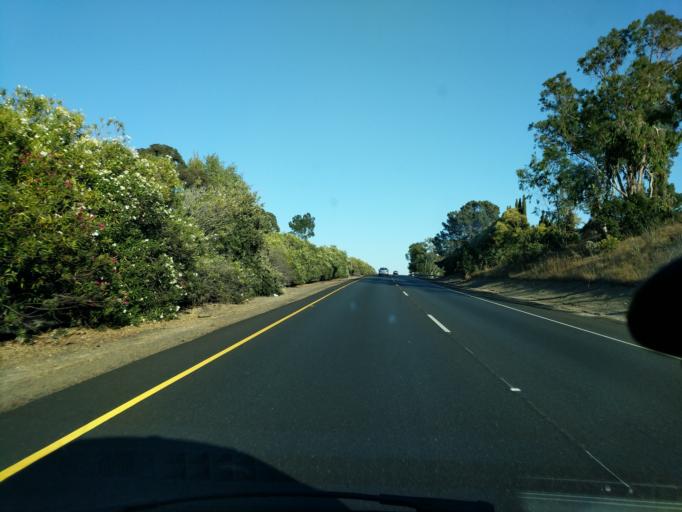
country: US
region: California
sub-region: Solano County
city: Benicia
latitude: 38.0638
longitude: -122.1607
